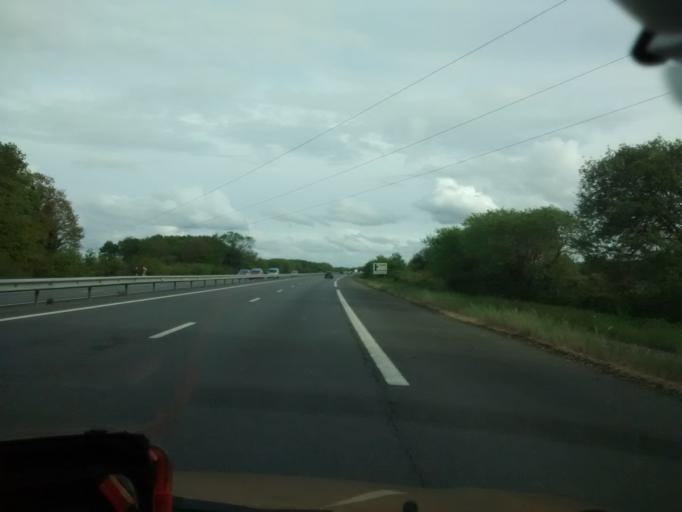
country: FR
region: Pays de la Loire
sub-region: Departement de la Loire-Atlantique
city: Prinquiau
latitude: 47.4047
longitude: -2.0110
